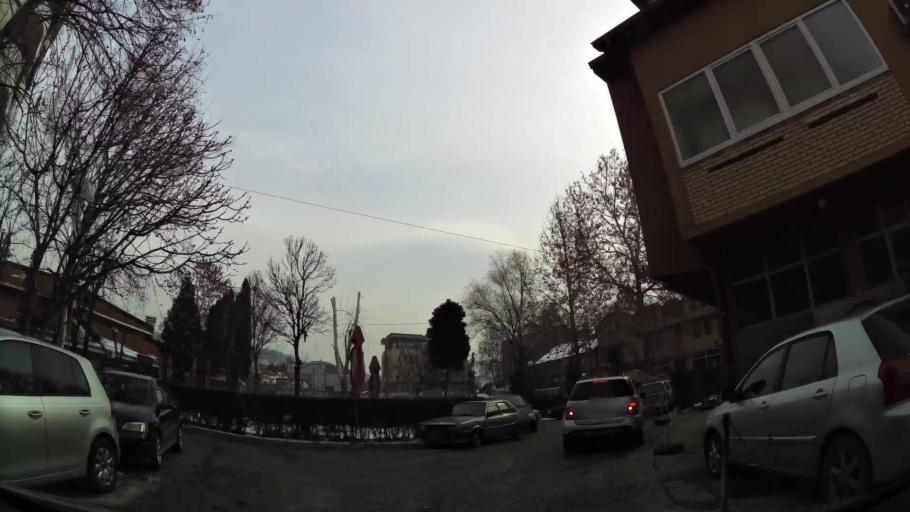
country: MK
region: Cair
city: Cair
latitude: 42.0085
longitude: 21.4423
